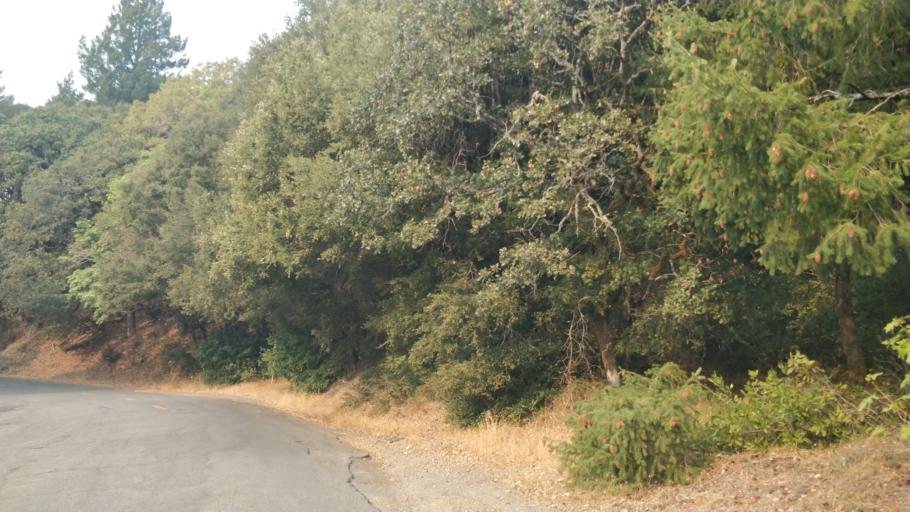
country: US
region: California
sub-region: Humboldt County
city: Rio Dell
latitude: 40.2444
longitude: -124.1227
